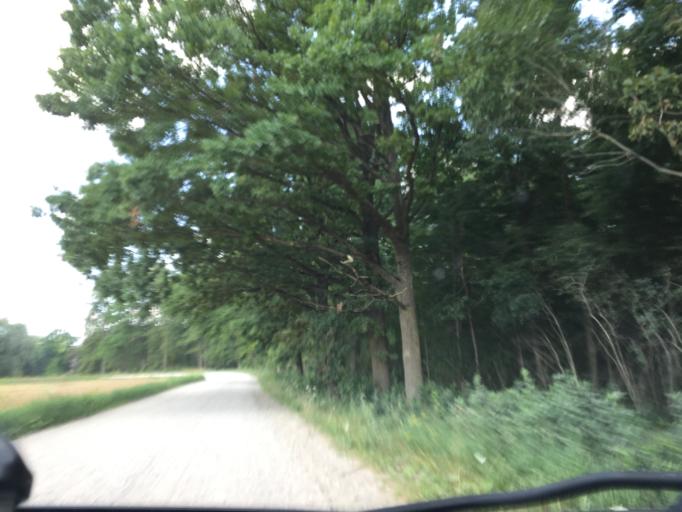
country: LT
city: Zagare
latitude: 56.3962
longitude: 23.2526
